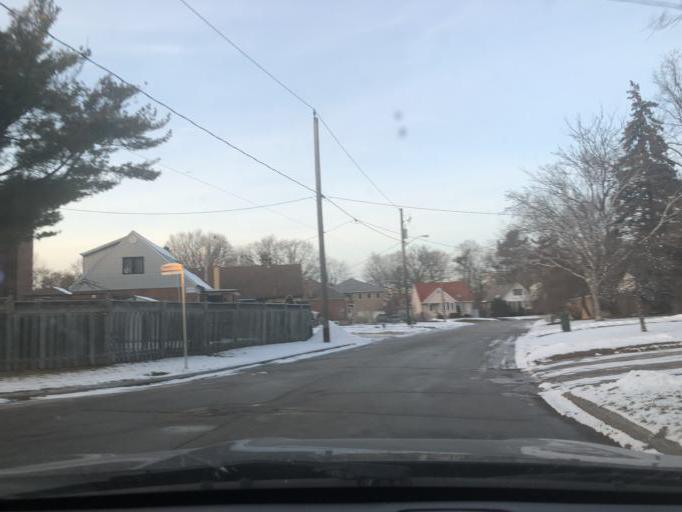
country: CA
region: Ontario
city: Toronto
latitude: 43.6998
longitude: -79.4905
